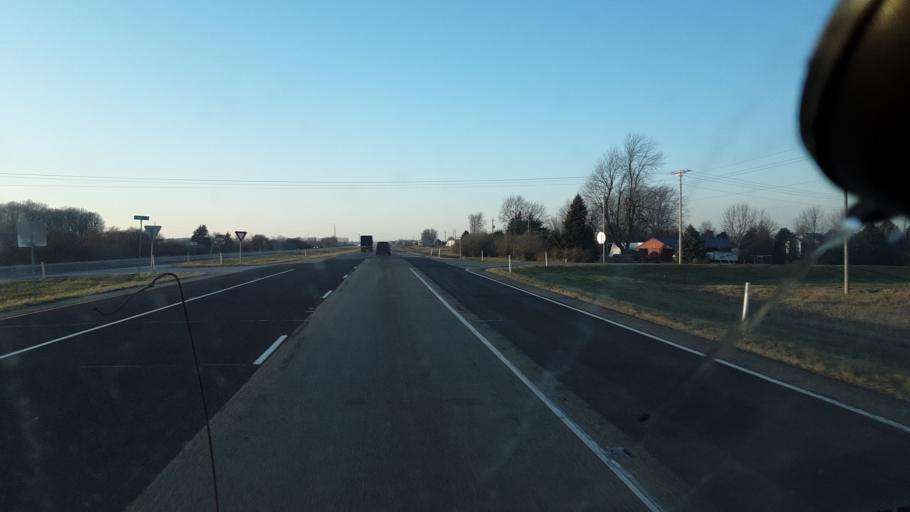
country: US
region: Indiana
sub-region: Allen County
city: New Haven
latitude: 41.0508
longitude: -84.9609
